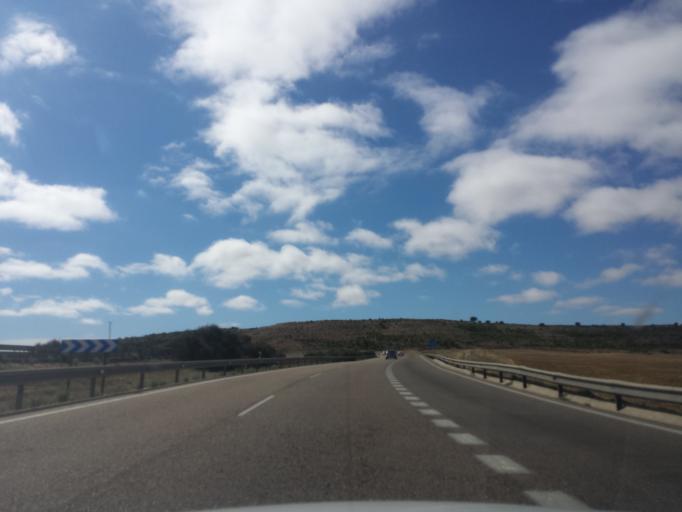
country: ES
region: Castille and Leon
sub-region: Provincia de Valladolid
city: Villardefrades
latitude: 41.7091
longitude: -5.2377
